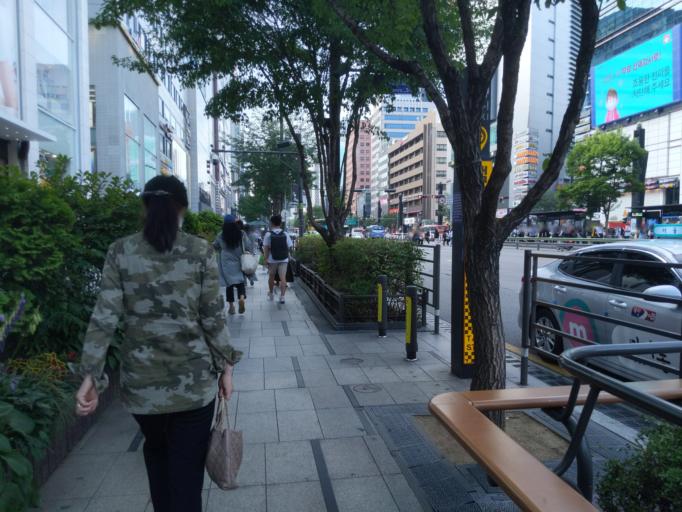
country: KR
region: Seoul
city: Seoul
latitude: 37.5004
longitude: 127.0264
